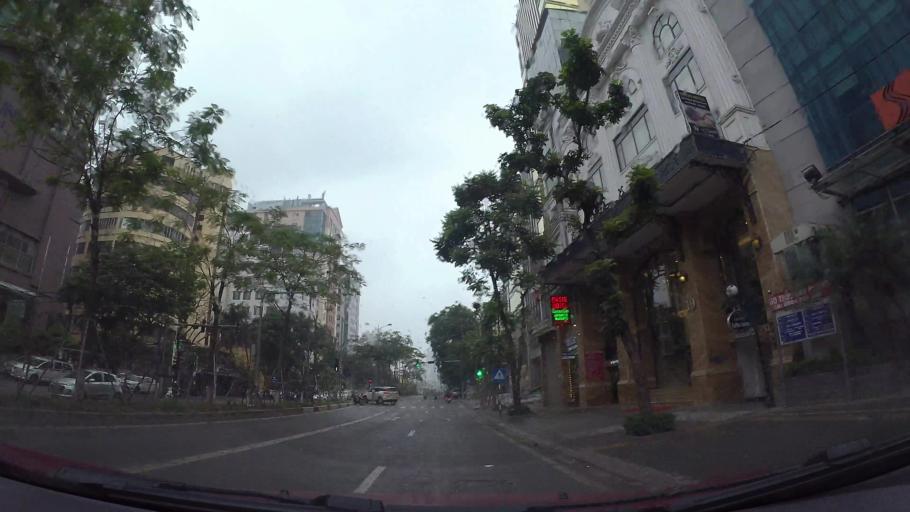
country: VN
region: Ha Noi
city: Dong Da
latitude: 21.0211
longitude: 105.8183
